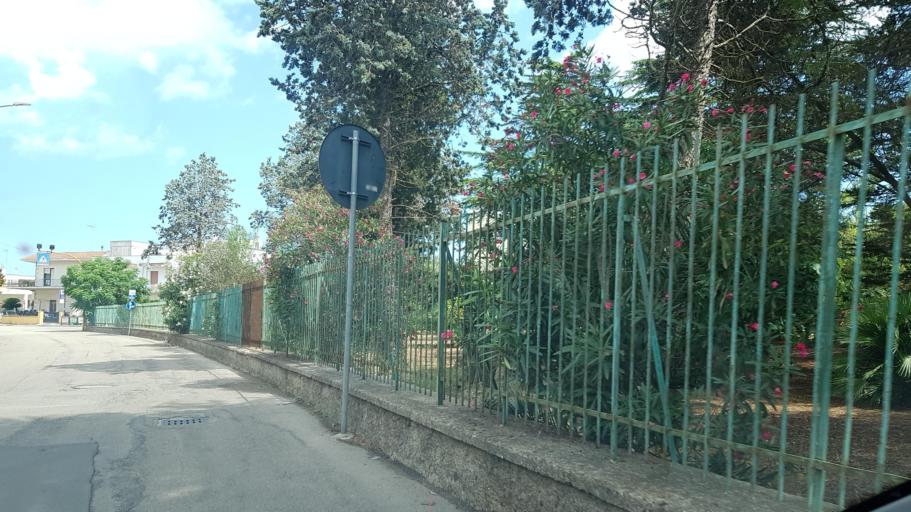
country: IT
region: Apulia
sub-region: Provincia di Lecce
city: Castrignano del Capo
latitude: 39.8346
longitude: 18.3510
